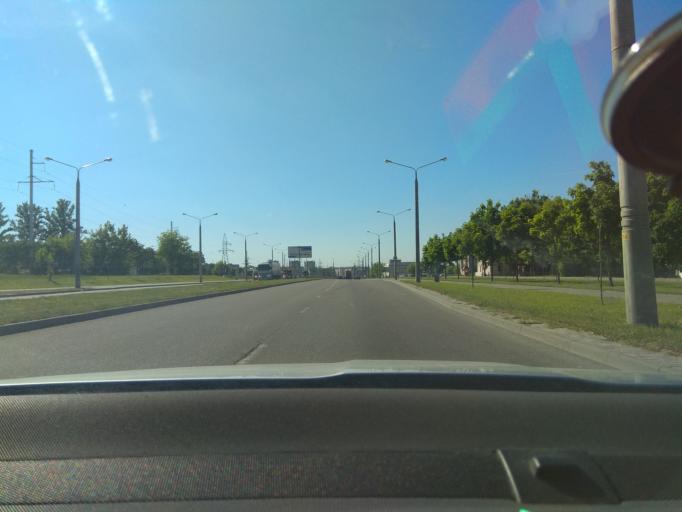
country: BY
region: Grodnenskaya
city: Hrodna
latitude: 53.6515
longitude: 23.7977
